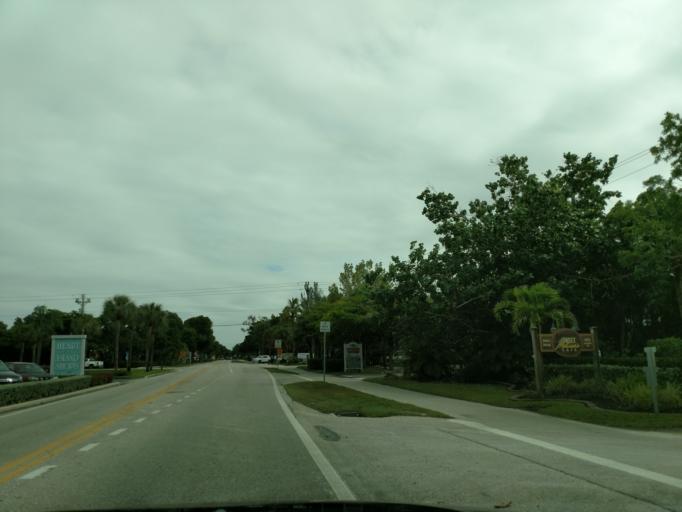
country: US
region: Florida
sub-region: Lee County
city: Sanibel
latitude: 26.4420
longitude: -82.0569
